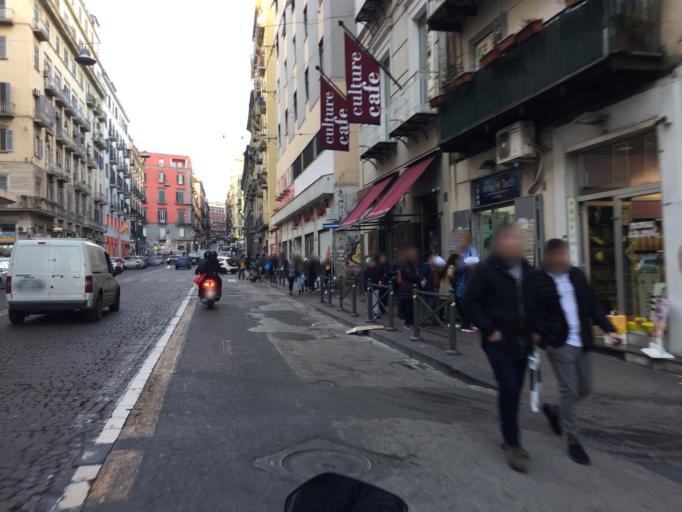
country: IT
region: Campania
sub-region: Provincia di Napoli
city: Napoli
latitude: 40.8442
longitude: 14.2521
